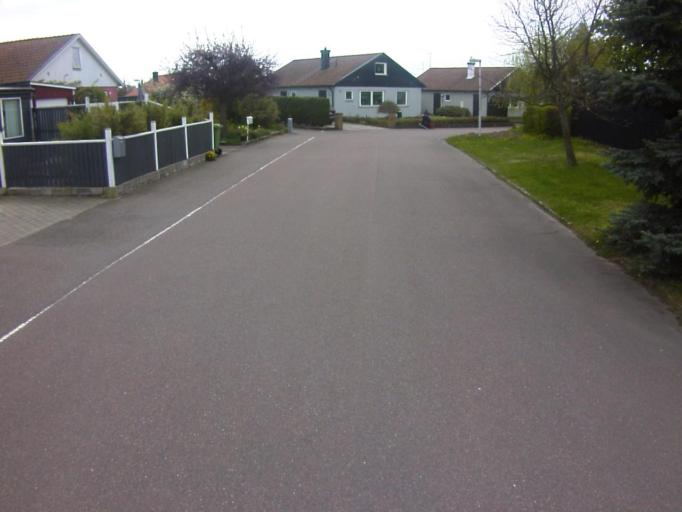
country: SE
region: Skane
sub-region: Kavlinge Kommun
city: Loddekopinge
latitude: 55.7562
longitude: 13.0031
